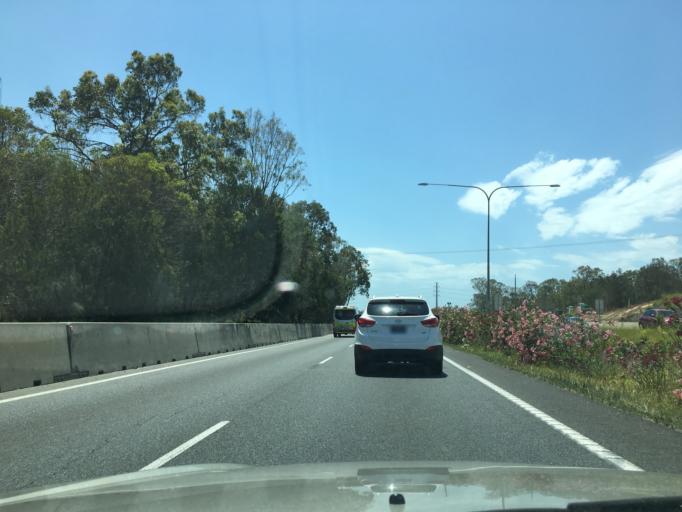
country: AU
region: Queensland
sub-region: Brisbane
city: Shorncliffe
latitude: -27.3703
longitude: 153.0968
